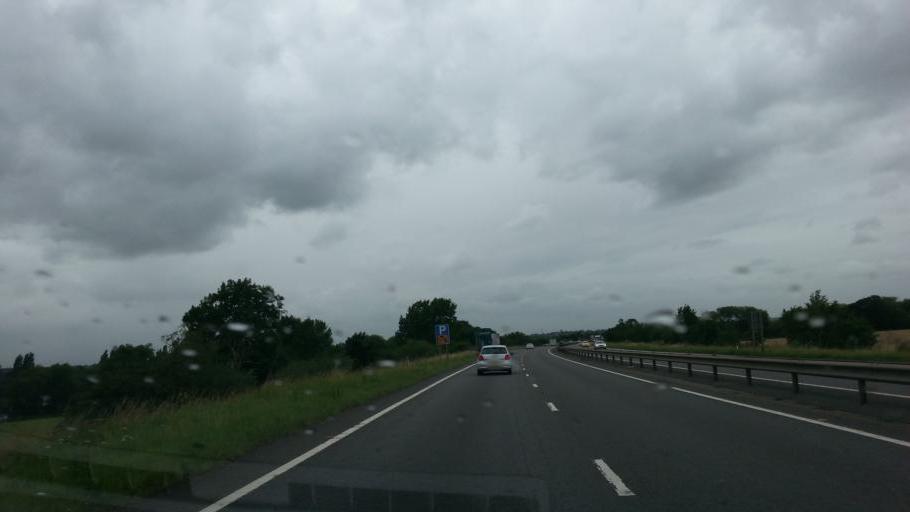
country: GB
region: England
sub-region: Nottinghamshire
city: Newark on Trent
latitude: 53.1045
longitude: -0.8049
